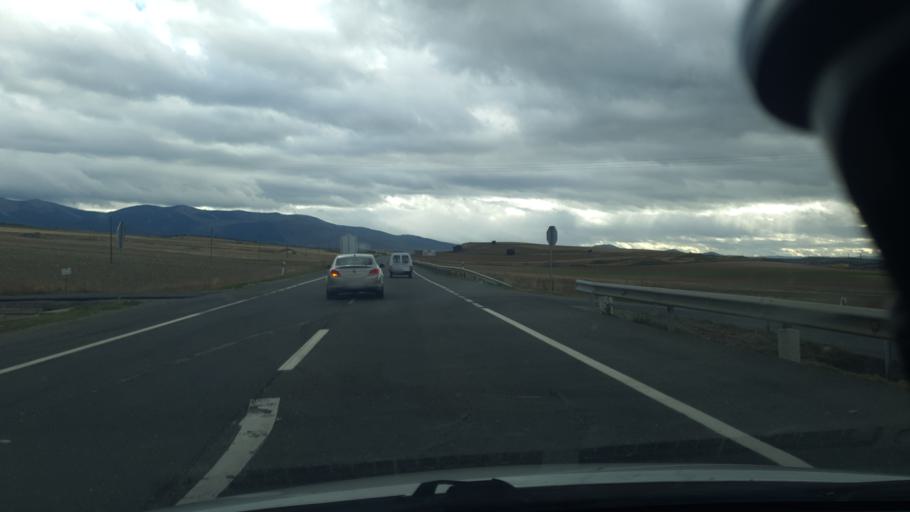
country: ES
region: Castille and Leon
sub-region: Provincia de Segovia
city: Segovia
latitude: 40.9158
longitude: -4.1579
